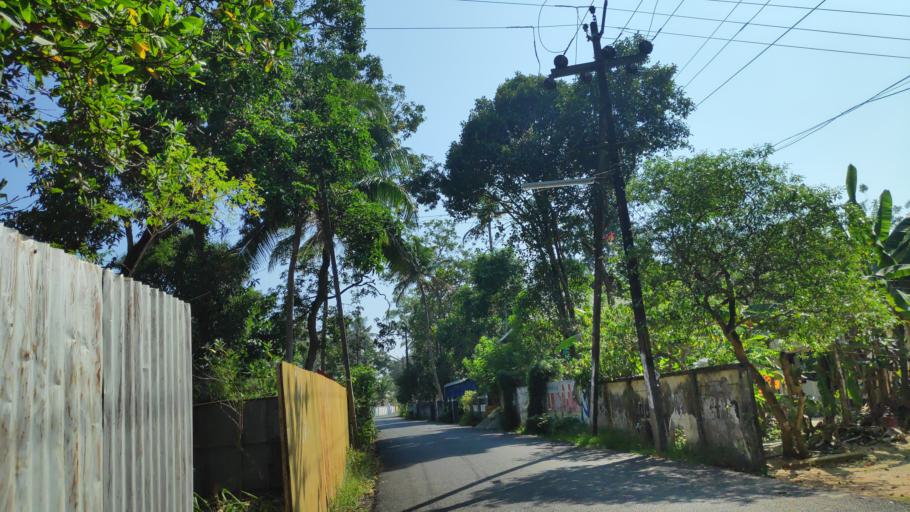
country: IN
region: Kerala
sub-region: Alappuzha
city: Alleppey
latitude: 9.5494
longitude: 76.3198
